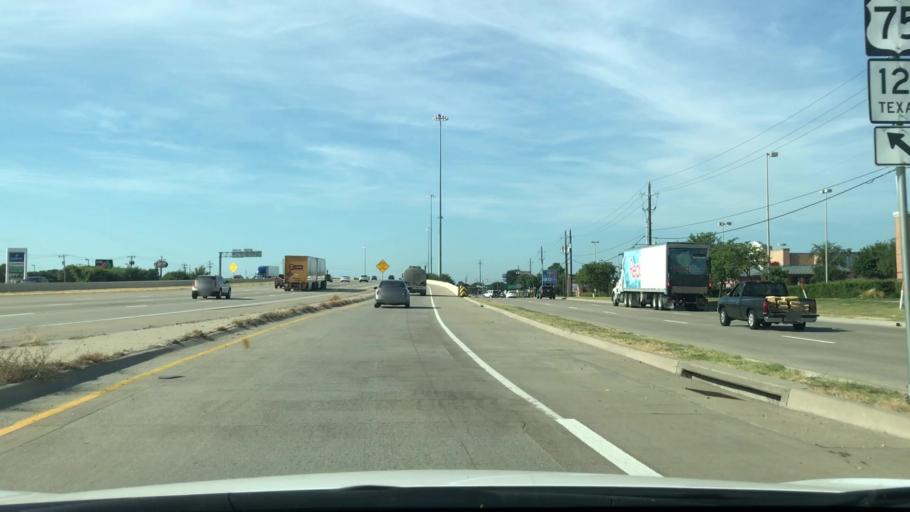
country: US
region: Texas
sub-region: Collin County
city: McKinney
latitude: 33.2207
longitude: -96.6356
